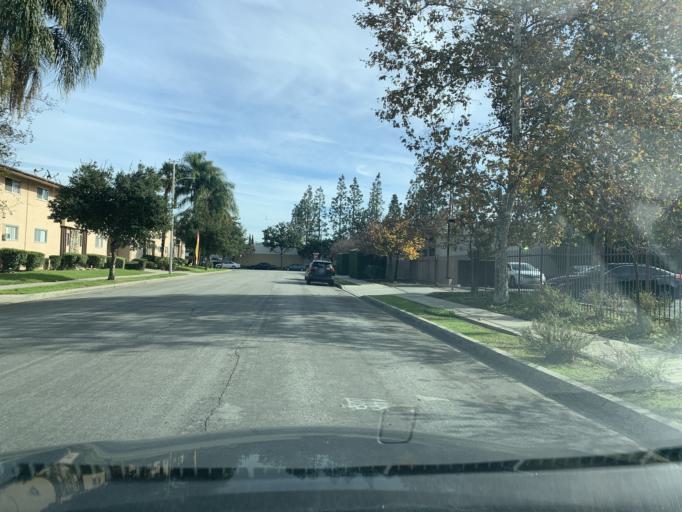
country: US
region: California
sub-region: Los Angeles County
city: West Covina
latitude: 34.0735
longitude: -117.9400
